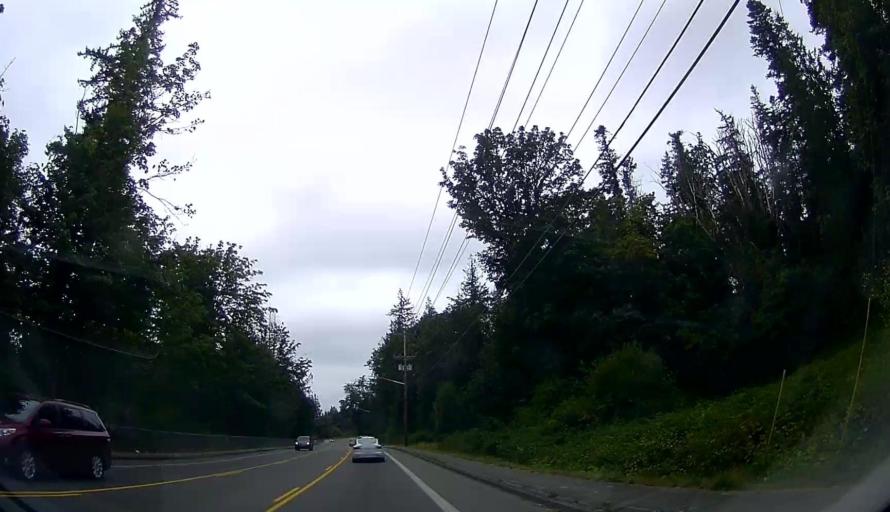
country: US
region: Washington
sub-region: Snohomish County
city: Marysville
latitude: 48.0482
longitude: -122.2151
